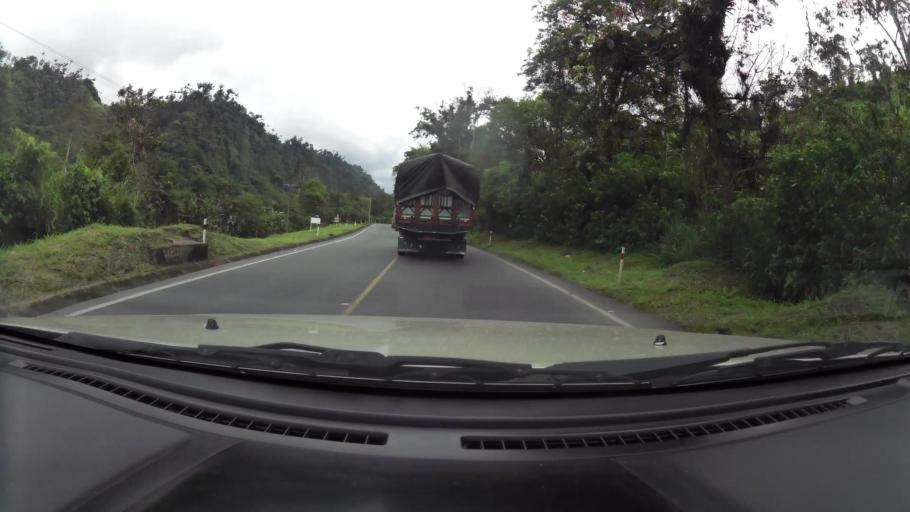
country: EC
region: Santo Domingo de los Tsachilas
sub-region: Canton Santo Domingo de los Colorados
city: Santo Domingo de los Colorados
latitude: -0.2821
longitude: -79.0708
